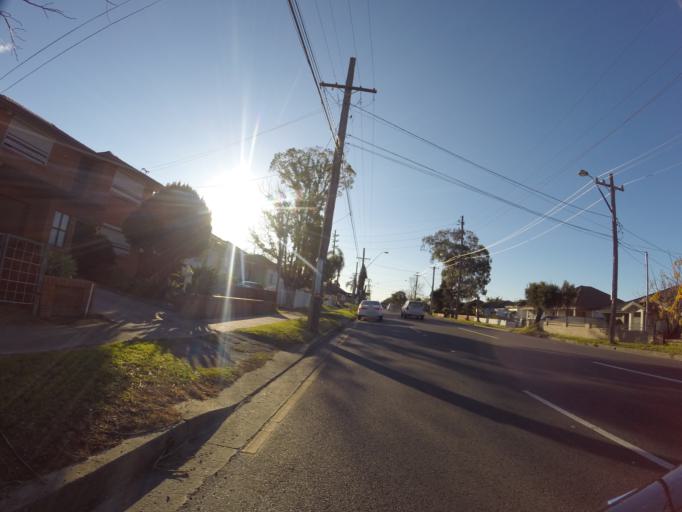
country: AU
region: New South Wales
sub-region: Fairfield
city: Fairfield Heights
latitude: -33.8616
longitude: 150.9527
